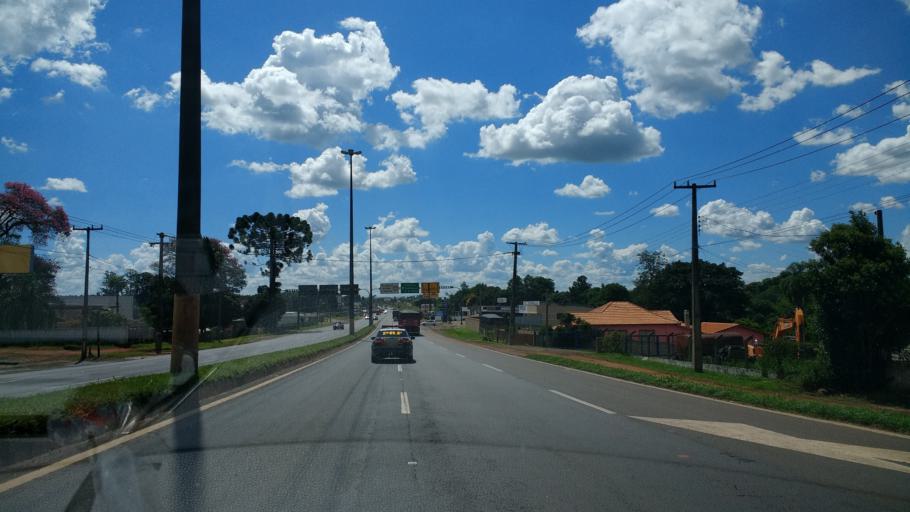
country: BR
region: Parana
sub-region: Ponta Grossa
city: Ponta Grossa
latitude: -25.0620
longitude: -50.2164
